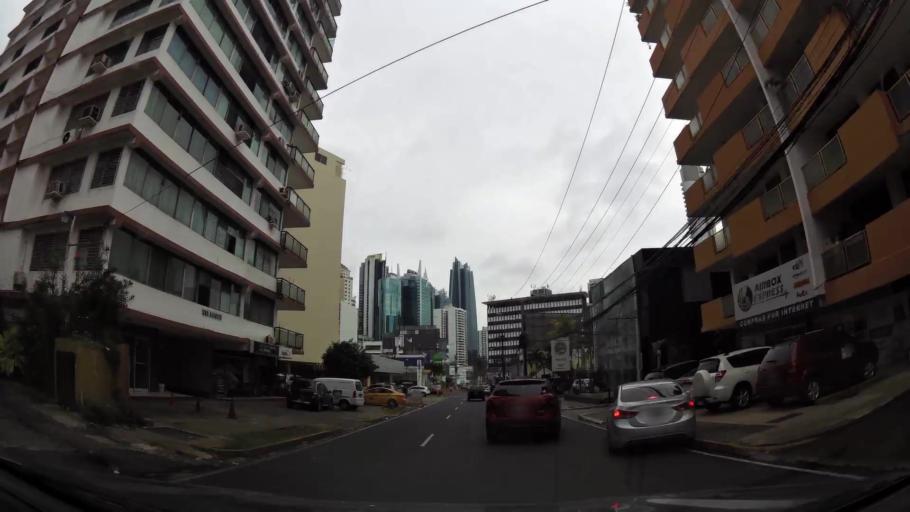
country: PA
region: Panama
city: Panama
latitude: 8.9868
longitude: -79.5256
